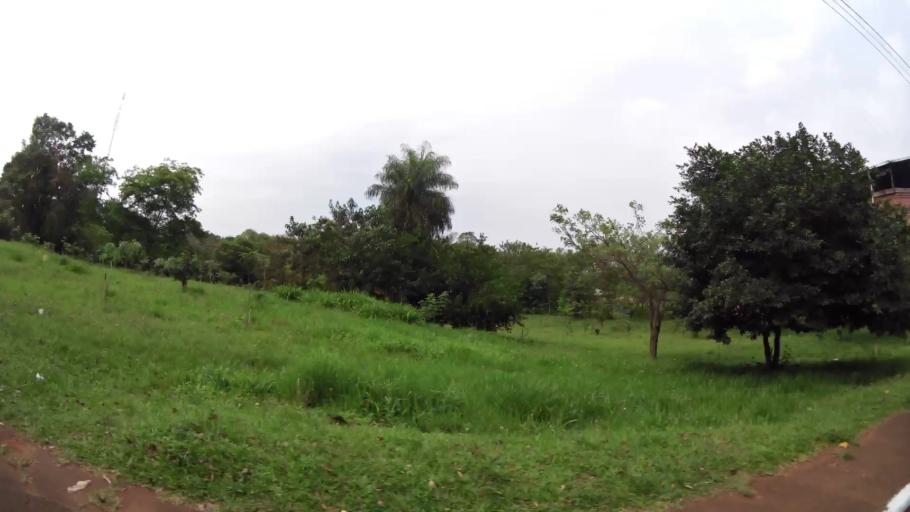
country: PY
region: Alto Parana
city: Presidente Franco
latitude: -25.5478
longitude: -54.6167
